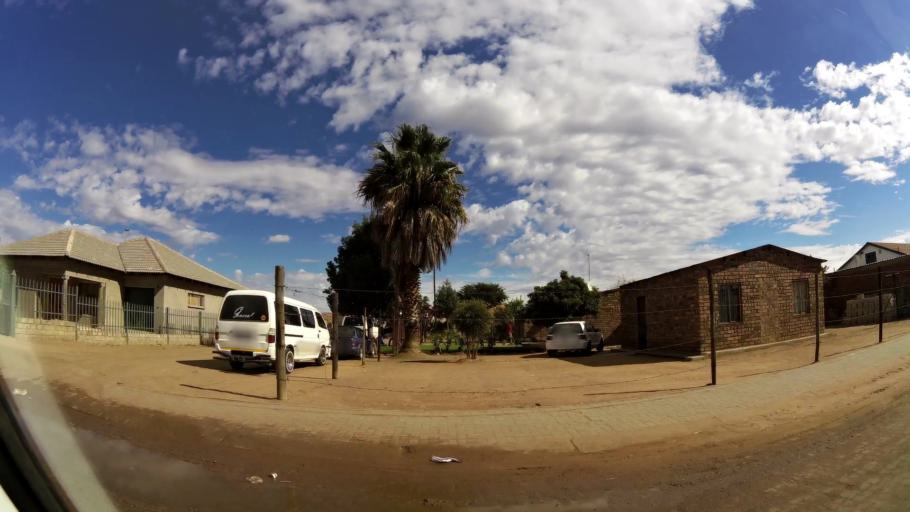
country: ZA
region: Limpopo
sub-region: Waterberg District Municipality
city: Bela-Bela
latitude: -24.8868
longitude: 28.3110
